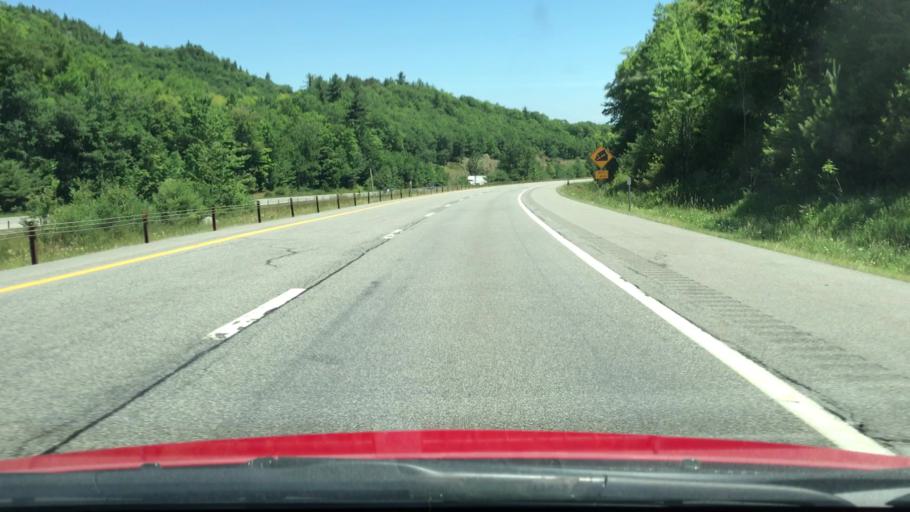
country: US
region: New York
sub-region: Essex County
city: Elizabethtown
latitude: 44.1885
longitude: -73.5624
